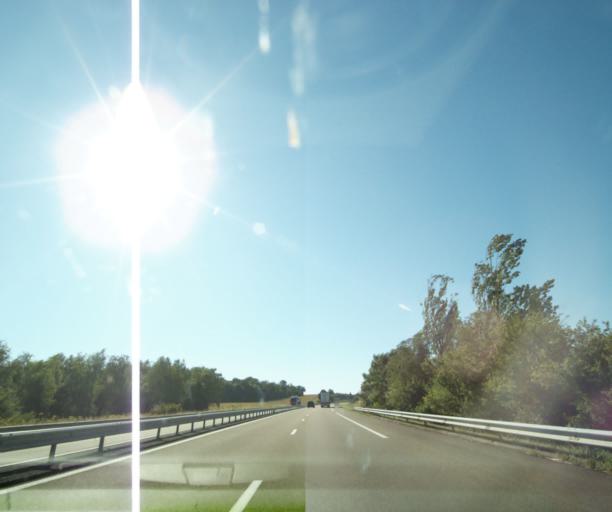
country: FR
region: Champagne-Ardenne
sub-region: Departement de l'Aube
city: Vendeuvre-sur-Barse
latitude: 48.1679
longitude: 4.5849
